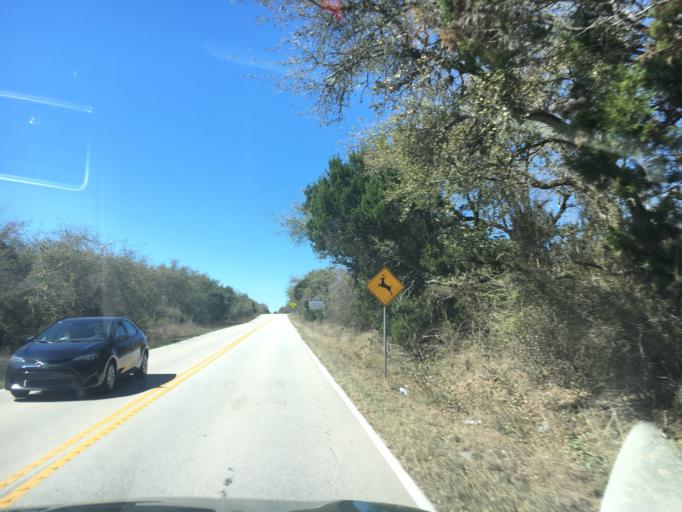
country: US
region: Texas
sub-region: Hays County
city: Dripping Springs
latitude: 30.2882
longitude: -98.0681
